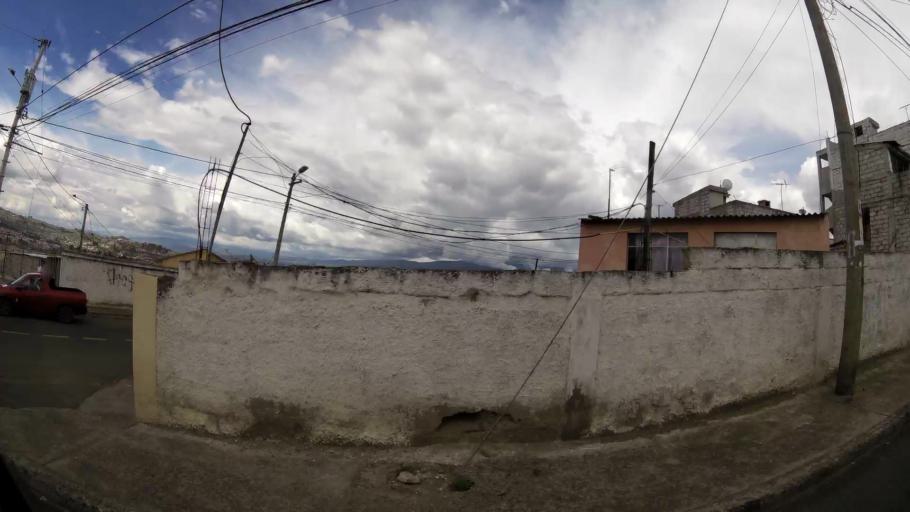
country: EC
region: Tungurahua
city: Ambato
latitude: -1.2542
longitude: -78.6178
